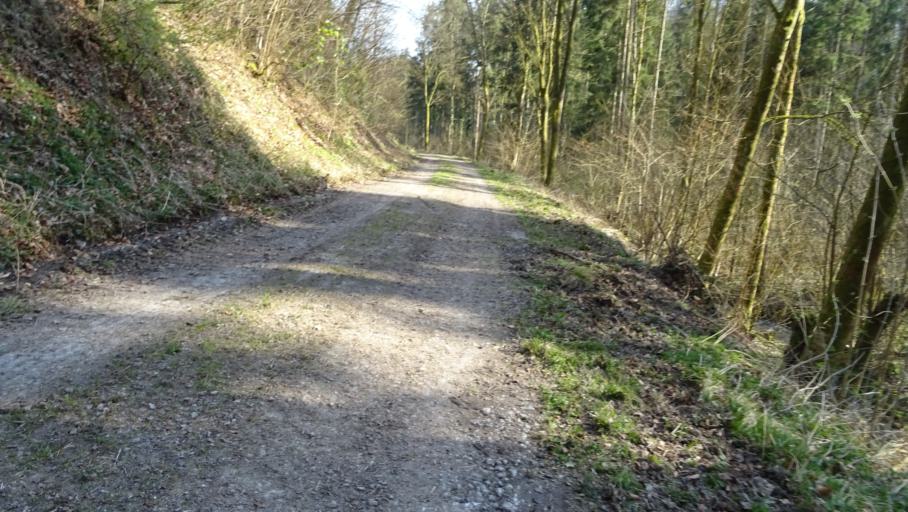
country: DE
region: Baden-Wuerttemberg
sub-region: Regierungsbezirk Stuttgart
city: Roigheim
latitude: 49.3771
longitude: 9.3530
